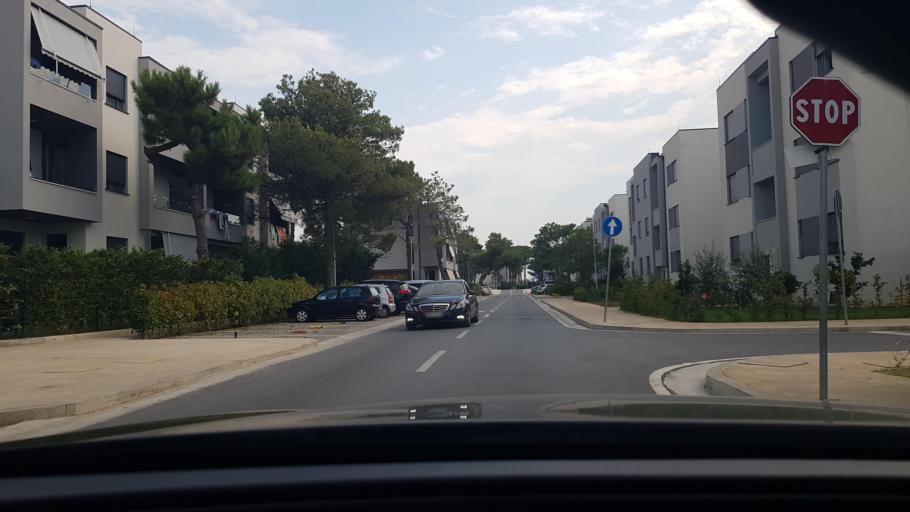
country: AL
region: Durres
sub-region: Rrethi i Durresit
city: Katundi i Ri
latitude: 41.4900
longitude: 19.5131
